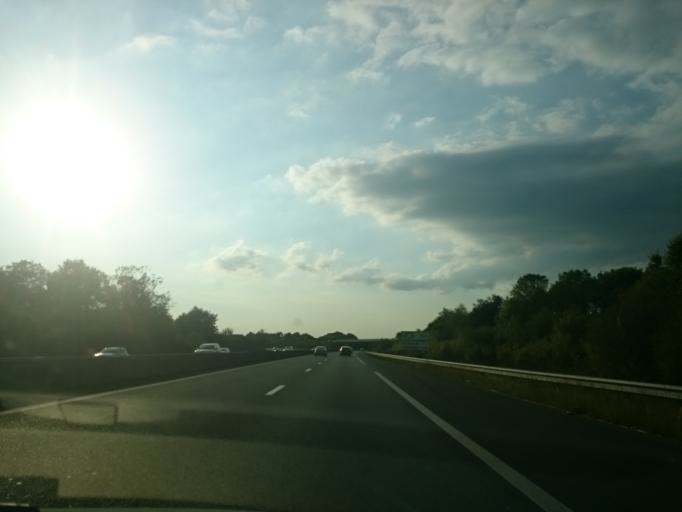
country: FR
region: Pays de la Loire
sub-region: Departement de la Loire-Atlantique
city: Savenay
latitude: 47.3712
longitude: -1.9242
